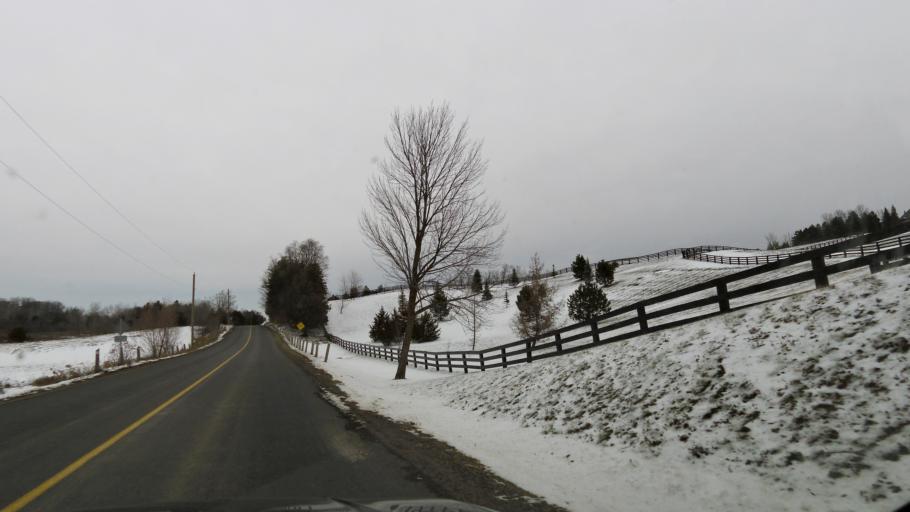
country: CA
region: Ontario
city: Bradford West Gwillimbury
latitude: 43.9598
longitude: -79.6408
